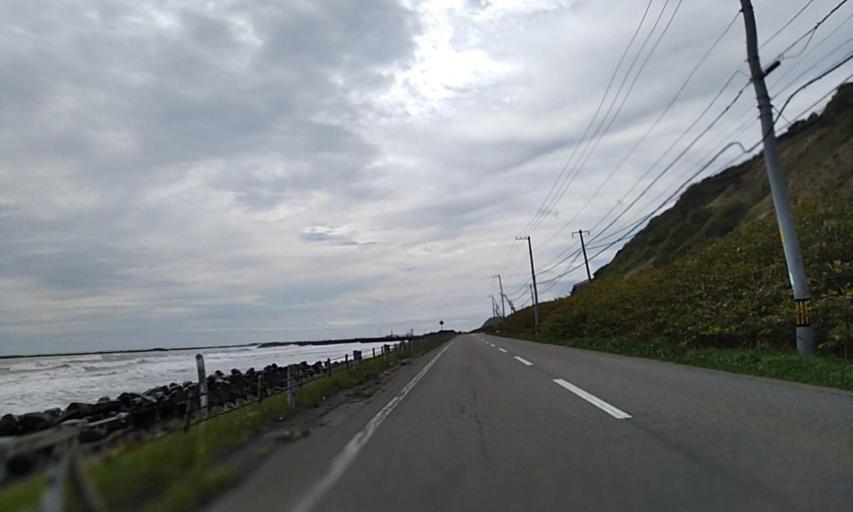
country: JP
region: Hokkaido
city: Kushiro
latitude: 42.8100
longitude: 143.8249
